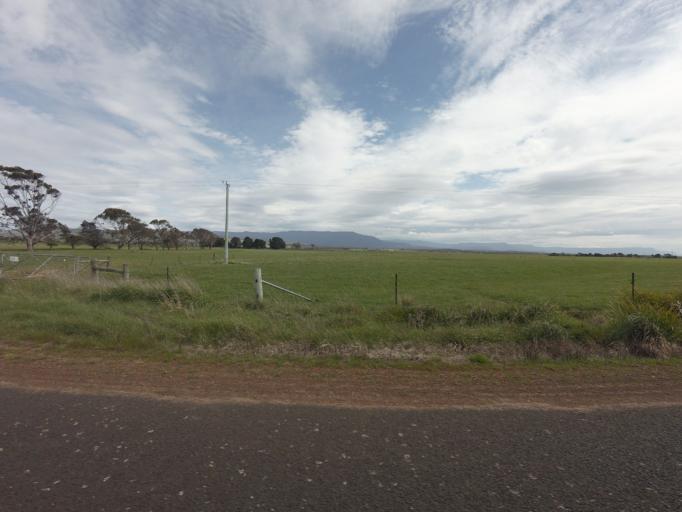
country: AU
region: Tasmania
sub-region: Northern Midlands
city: Evandale
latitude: -41.8521
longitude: 147.3405
